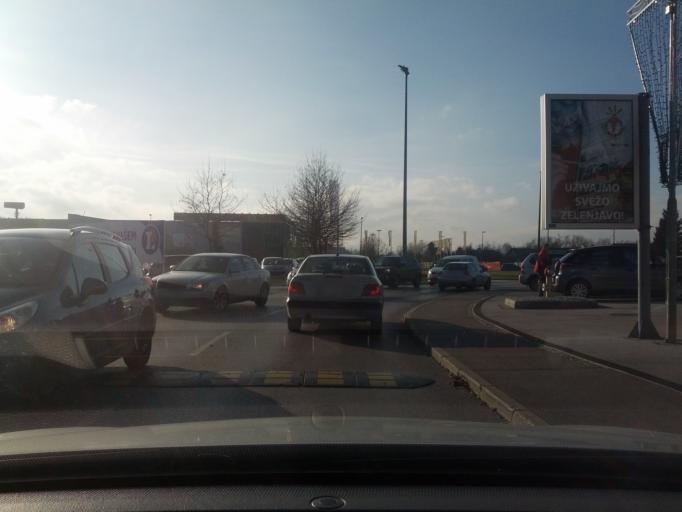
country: SI
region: Skofljica
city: Lavrica
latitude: 46.0213
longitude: 14.5359
